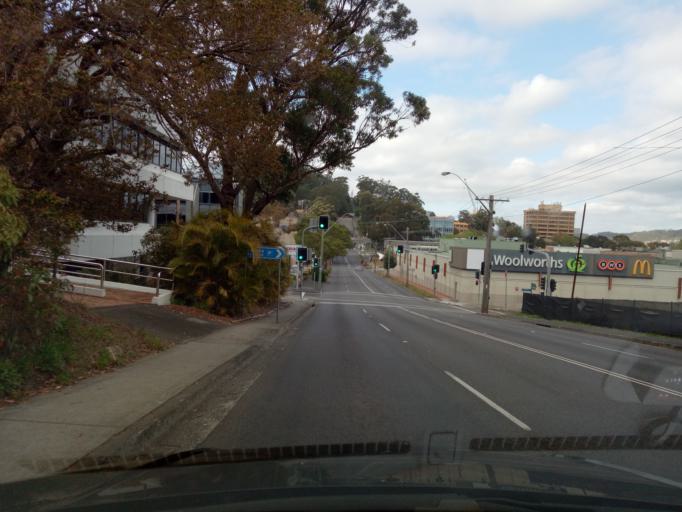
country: AU
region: New South Wales
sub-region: Gosford Shire
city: Gosford
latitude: -33.4249
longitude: 151.3447
